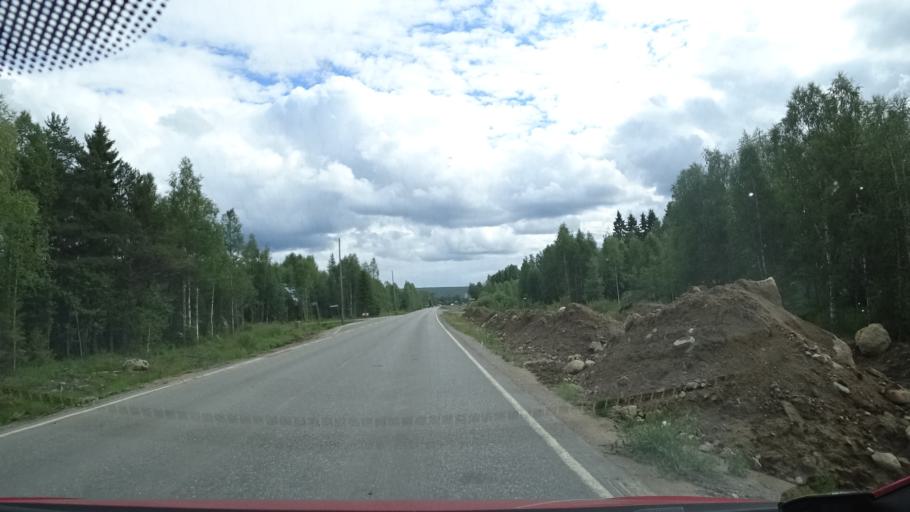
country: FI
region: Lapland
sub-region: Rovaniemi
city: Rovaniemi
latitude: 66.5303
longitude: 25.7375
